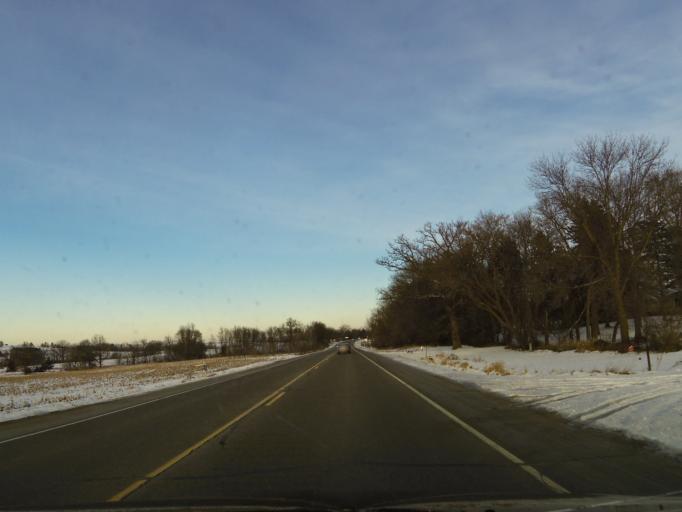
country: US
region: Wisconsin
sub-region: Polk County
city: Osceola
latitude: 45.3157
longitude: -92.7418
